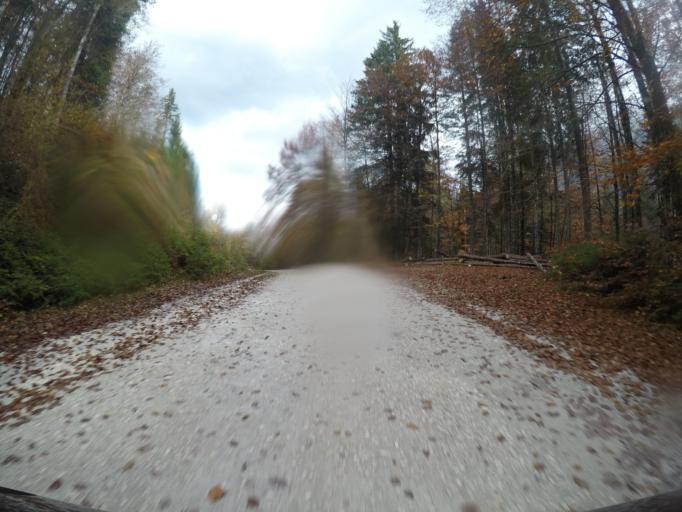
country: SI
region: Kranjska Gora
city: Mojstrana
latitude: 46.4252
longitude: 13.8664
